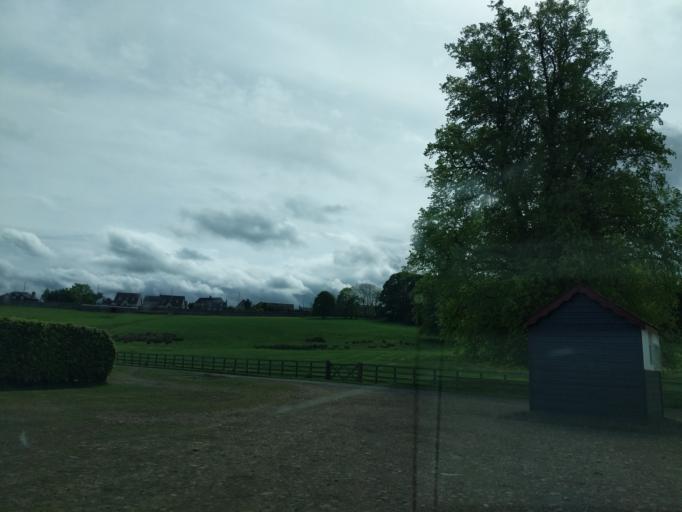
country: GB
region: Scotland
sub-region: The Scottish Borders
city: Lauder
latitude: 55.7203
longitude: -2.7422
